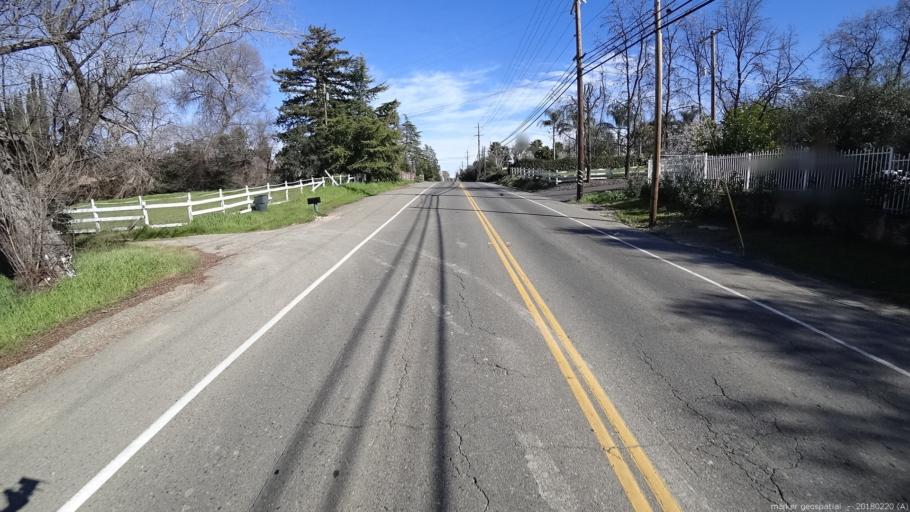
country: US
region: California
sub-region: Sacramento County
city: Folsom
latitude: 38.6997
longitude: -121.1995
